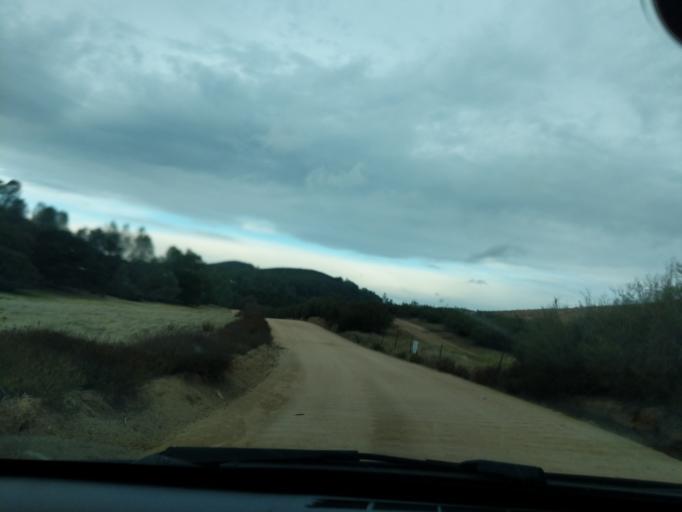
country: US
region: California
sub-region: Monterey County
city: Soledad
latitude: 36.5529
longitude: -121.2649
